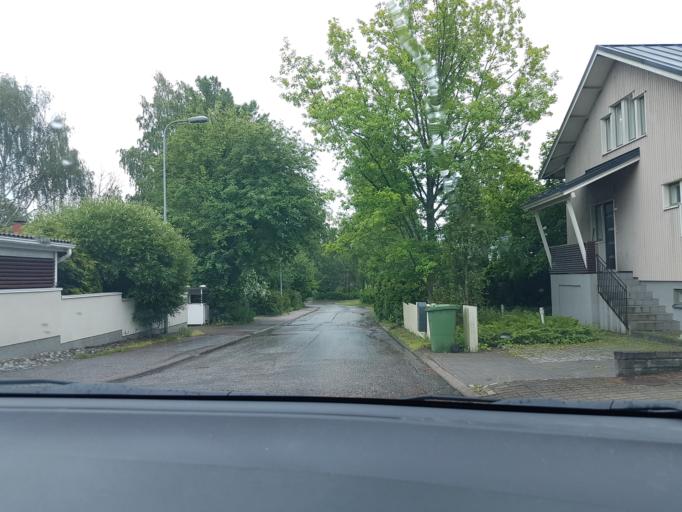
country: FI
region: Uusimaa
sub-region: Helsinki
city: Vantaa
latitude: 60.2328
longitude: 25.1002
